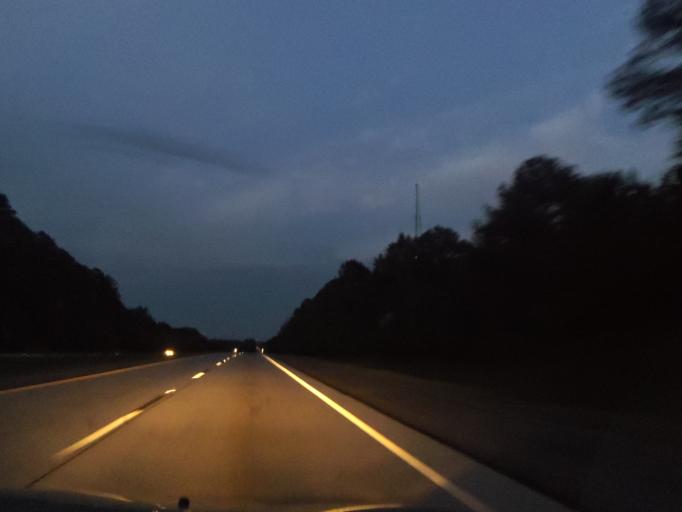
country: US
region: Georgia
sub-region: Columbia County
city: Appling
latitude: 33.5057
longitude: -82.3941
